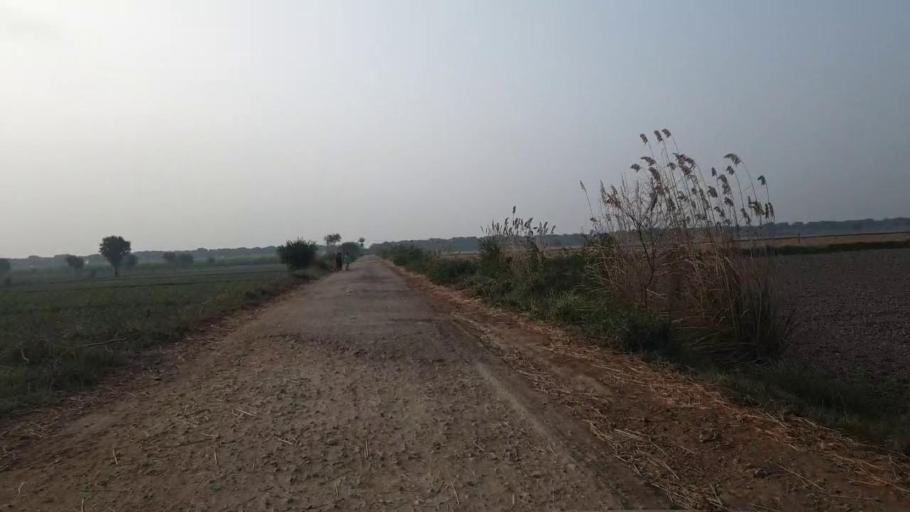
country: PK
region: Sindh
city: Tando Muhammad Khan
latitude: 25.1413
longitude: 68.6038
